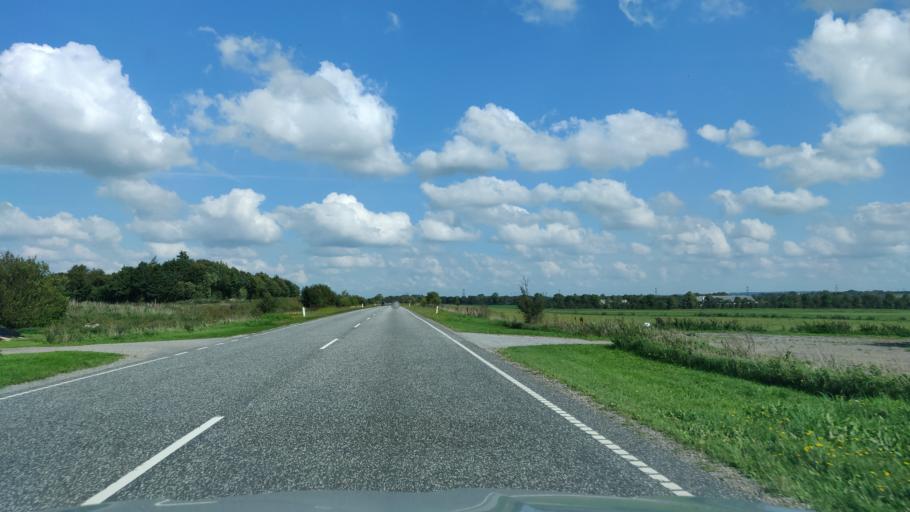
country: DK
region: North Denmark
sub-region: Vesthimmerland Kommune
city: Aars
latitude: 56.7837
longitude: 9.5906
